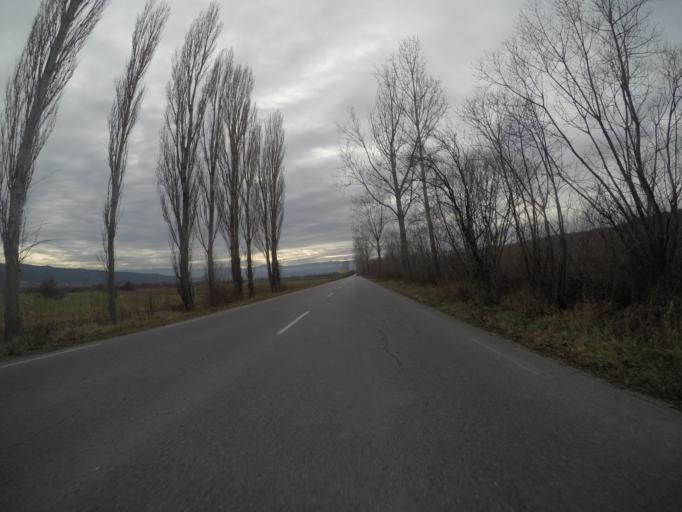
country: BG
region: Kyustendil
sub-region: Obshtina Rila
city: Rila
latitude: 42.1126
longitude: 23.1109
